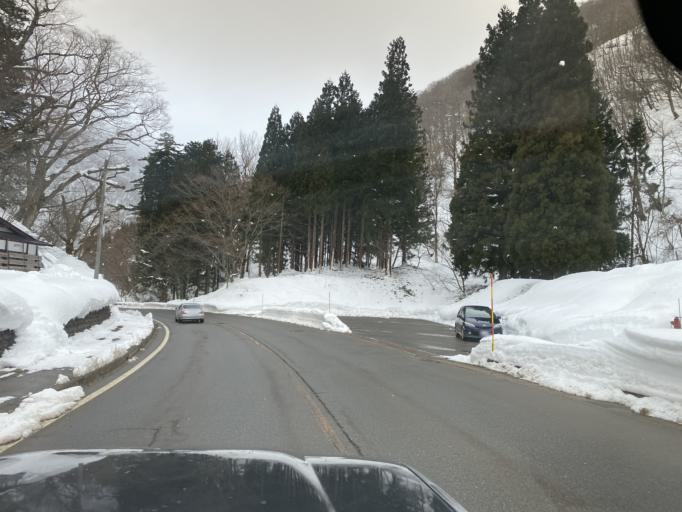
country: JP
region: Gifu
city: Takayama
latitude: 36.1553
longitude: 136.9069
